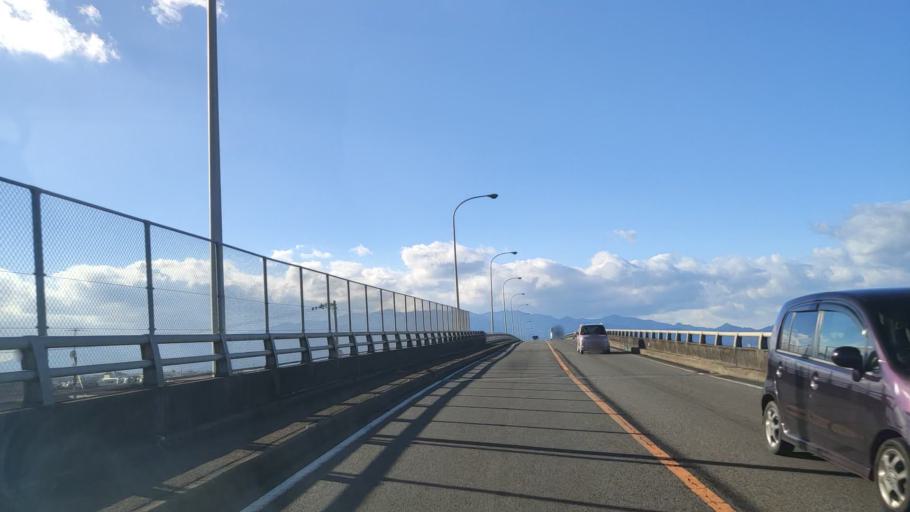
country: JP
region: Ehime
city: Saijo
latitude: 33.9155
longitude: 133.1353
